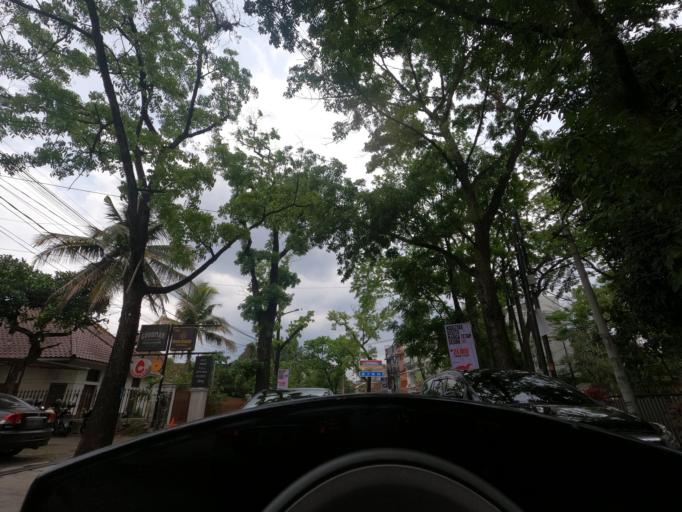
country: ID
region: West Java
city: Bandung
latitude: -6.9083
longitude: 107.6269
